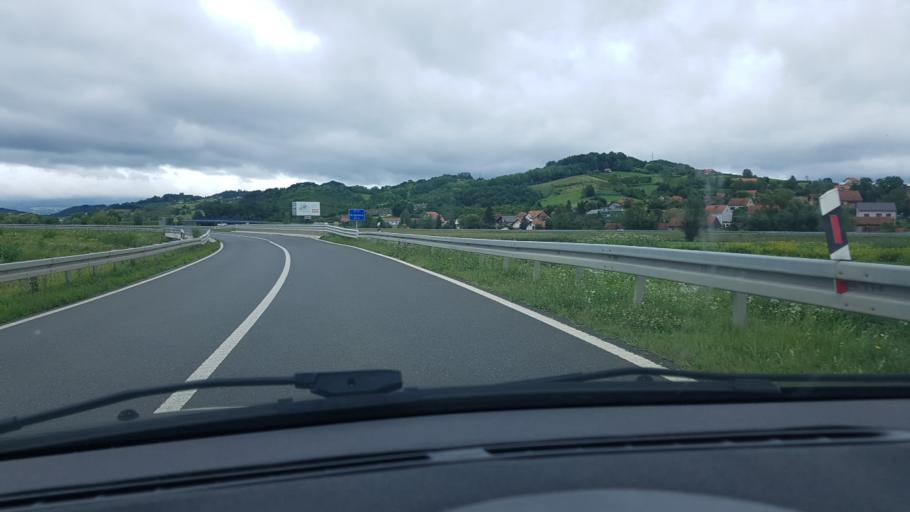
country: HR
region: Krapinsko-Zagorska
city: Zabok
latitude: 46.0728
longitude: 15.9156
